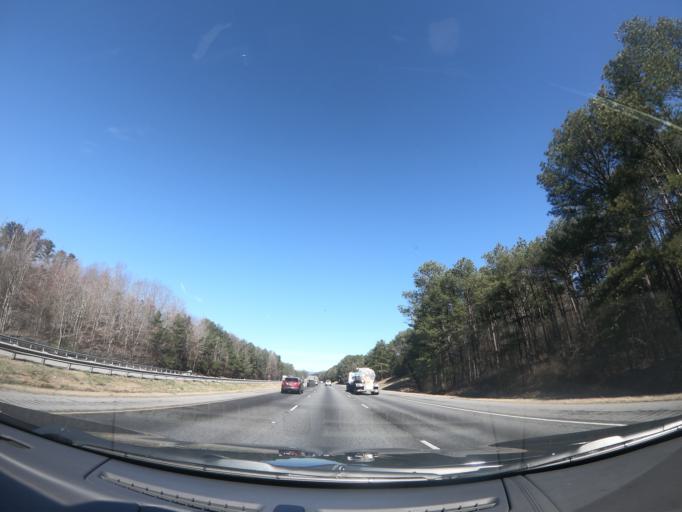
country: US
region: Georgia
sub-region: Gordon County
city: Calhoun
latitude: 34.6022
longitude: -84.9571
